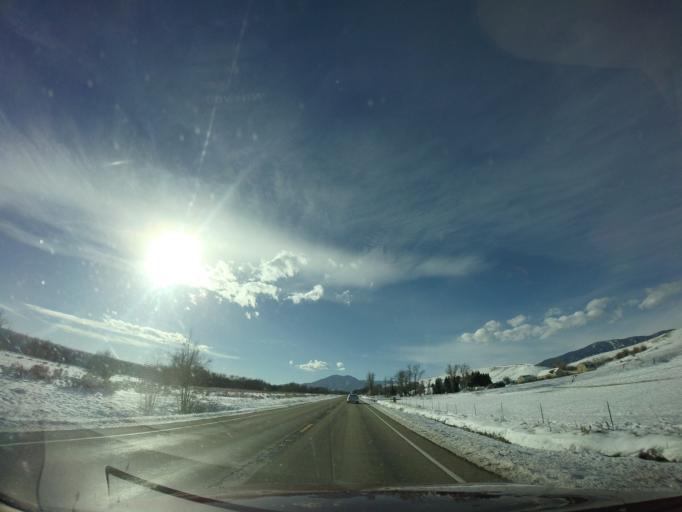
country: US
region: Montana
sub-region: Carbon County
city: Red Lodge
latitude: 45.2397
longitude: -109.2363
